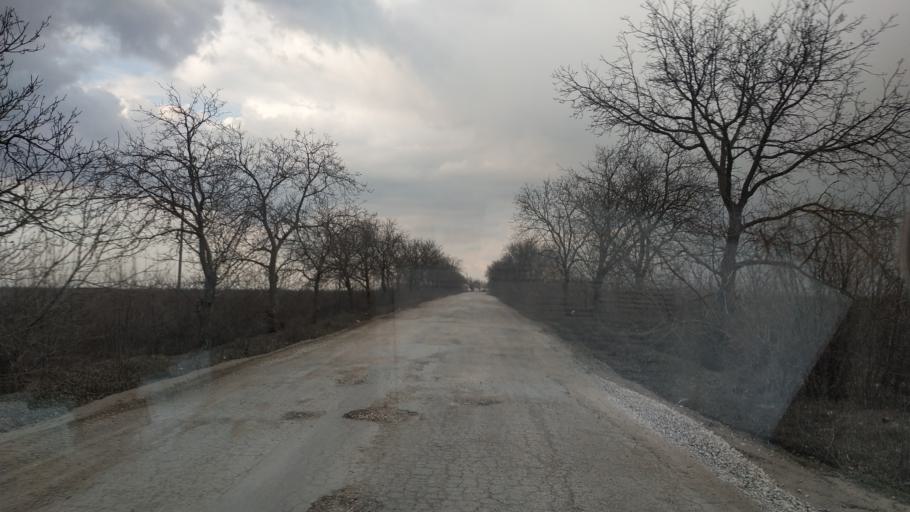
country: MD
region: Telenesti
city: Grigoriopol
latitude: 47.0439
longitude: 29.2940
